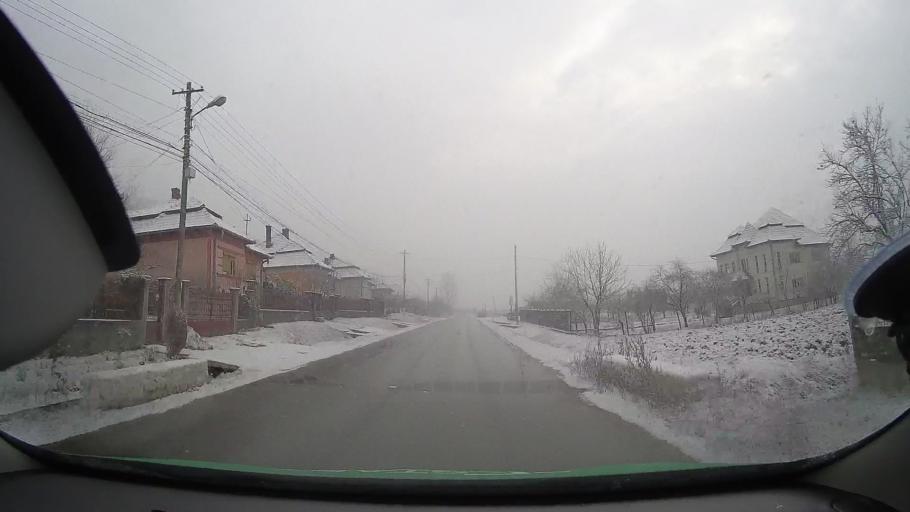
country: RO
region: Alba
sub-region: Comuna Lopadea Noua
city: Lopadea Noua
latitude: 46.3056
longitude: 23.7991
